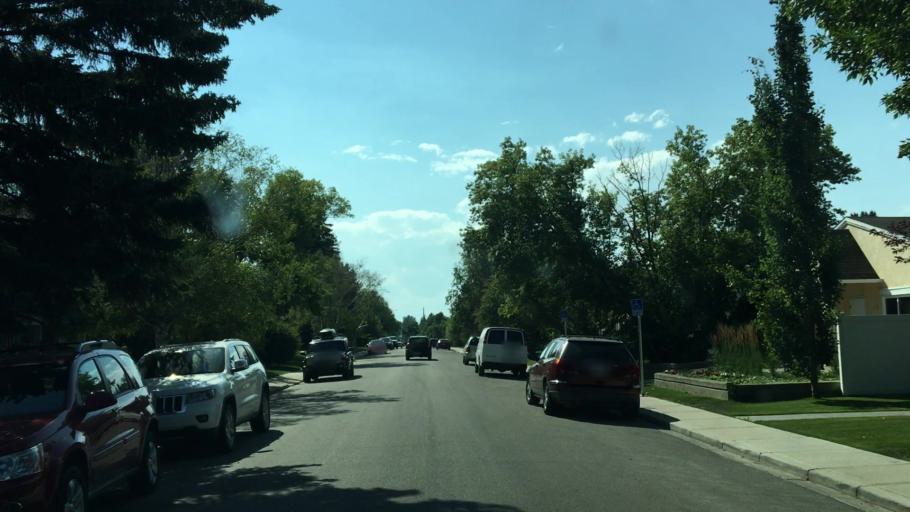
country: CA
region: Alberta
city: Calgary
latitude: 51.0796
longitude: -114.0680
